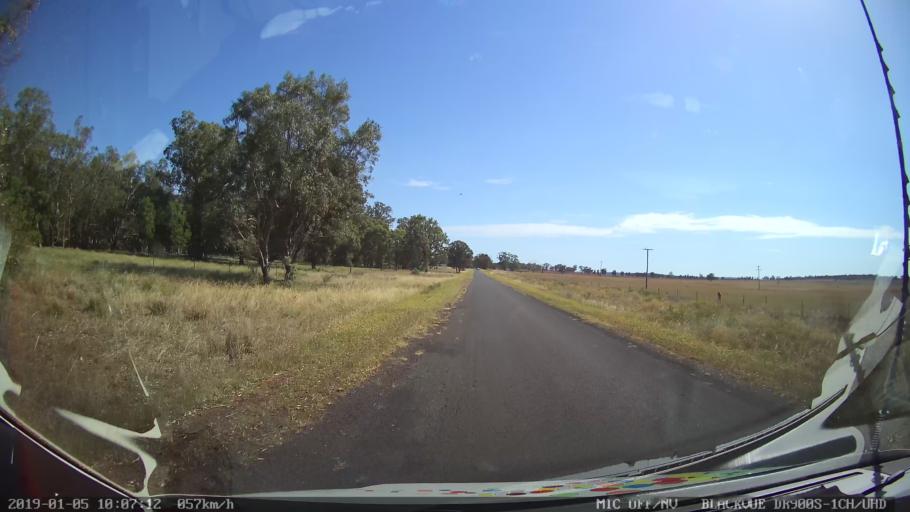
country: AU
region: New South Wales
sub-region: Gilgandra
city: Gilgandra
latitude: -31.6512
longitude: 148.8735
